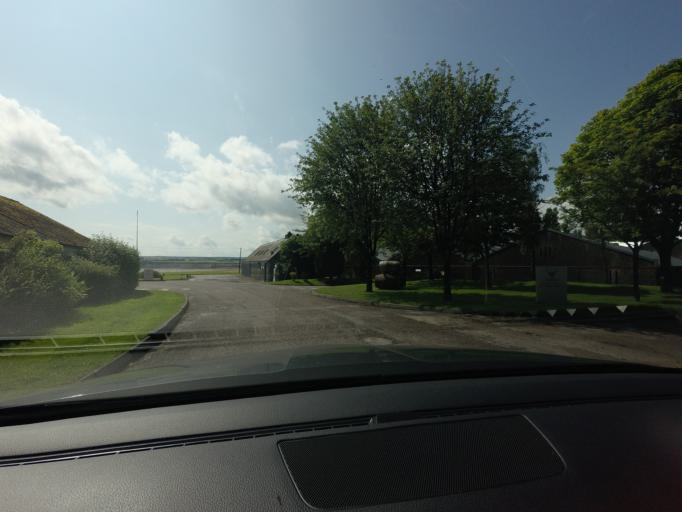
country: GB
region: Scotland
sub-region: Highland
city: Alness
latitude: 57.6883
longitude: -4.2404
